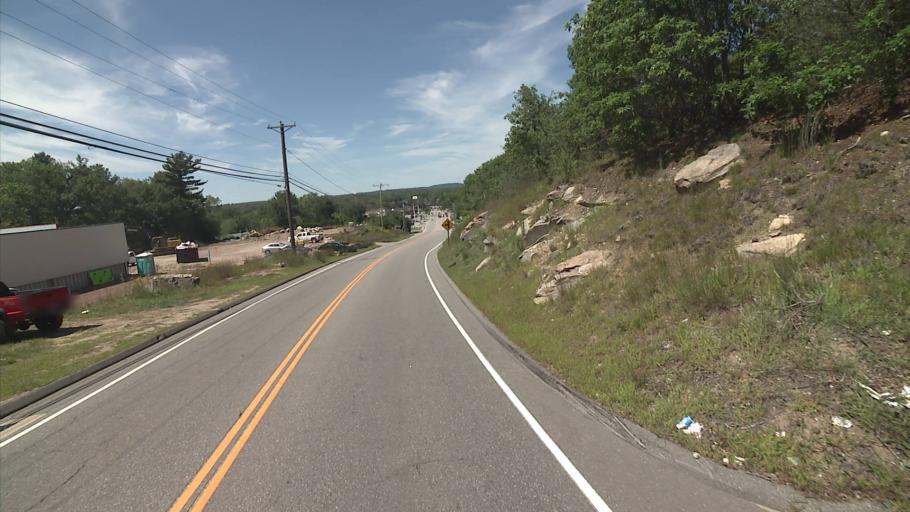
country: US
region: Connecticut
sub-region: Windham County
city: Killingly Center
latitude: 41.8390
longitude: -71.8725
